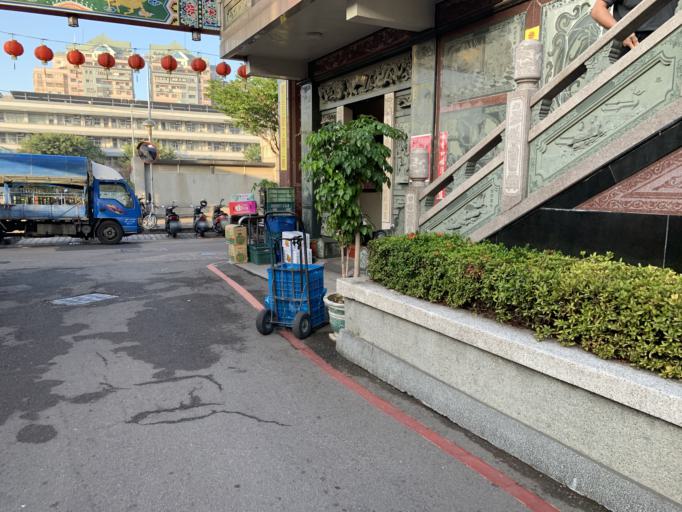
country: TW
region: Taiwan
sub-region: Taichung City
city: Taichung
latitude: 24.1380
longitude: 120.6388
